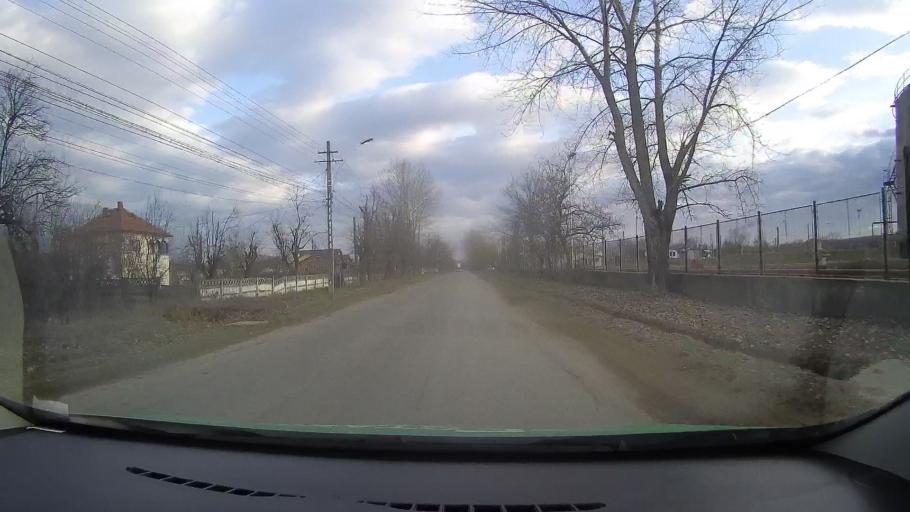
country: RO
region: Dambovita
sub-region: Municipiul Moreni
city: Moreni
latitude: 44.9651
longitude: 25.6549
